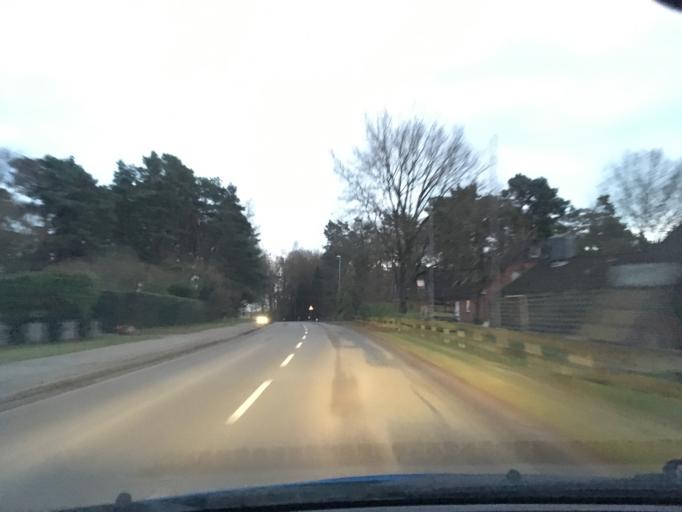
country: DE
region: Lower Saxony
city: Barum
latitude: 53.3480
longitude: 10.4151
